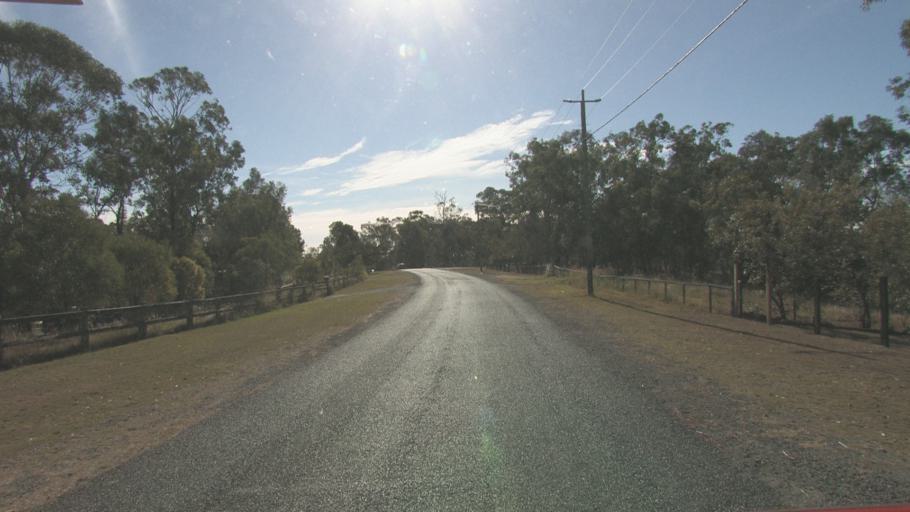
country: AU
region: Queensland
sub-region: Ipswich
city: Springfield Lakes
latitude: -27.7030
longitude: 152.9285
